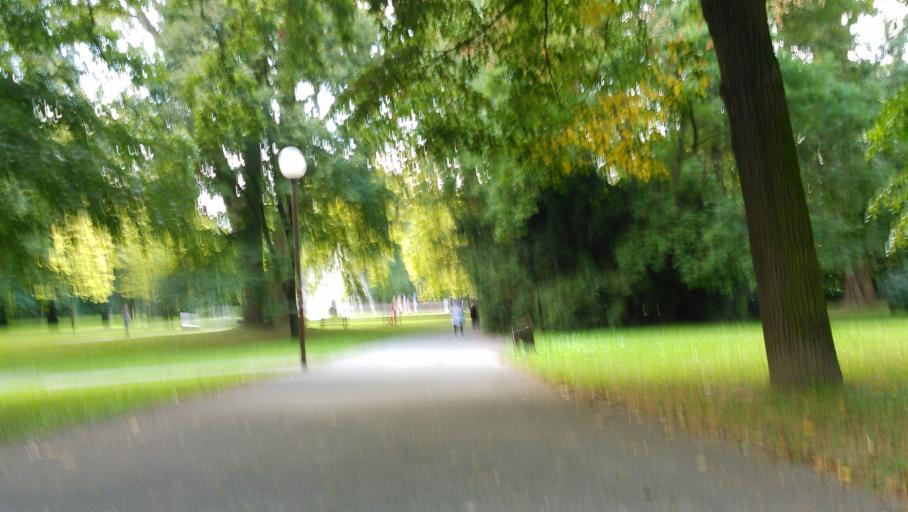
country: SK
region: Bratislavsky
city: Bratislava
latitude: 48.1338
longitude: 17.1131
